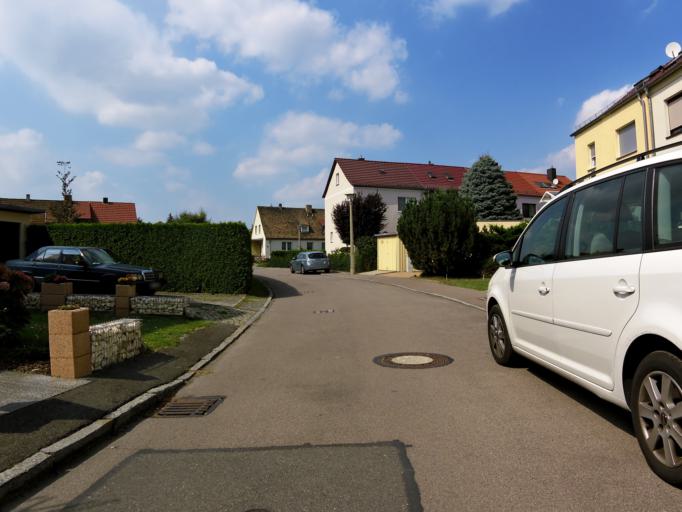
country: DE
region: Saxony
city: Leipzig
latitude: 51.3786
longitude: 12.3386
